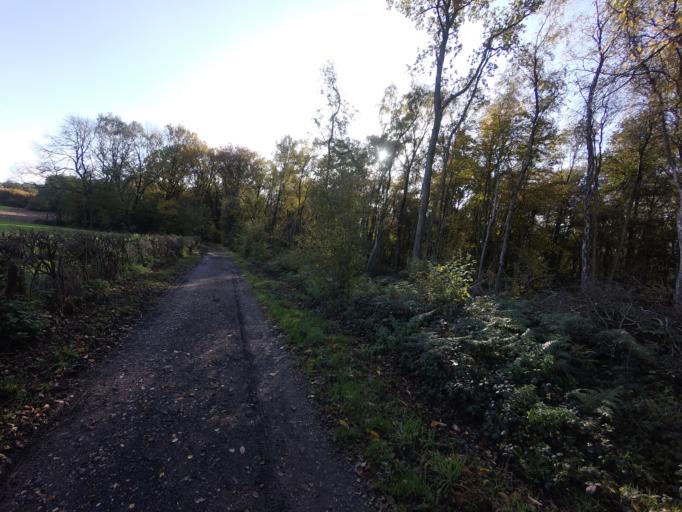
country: NL
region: Limburg
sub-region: Eijsden-Margraten
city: Margraten
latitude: 50.7914
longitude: 5.8683
